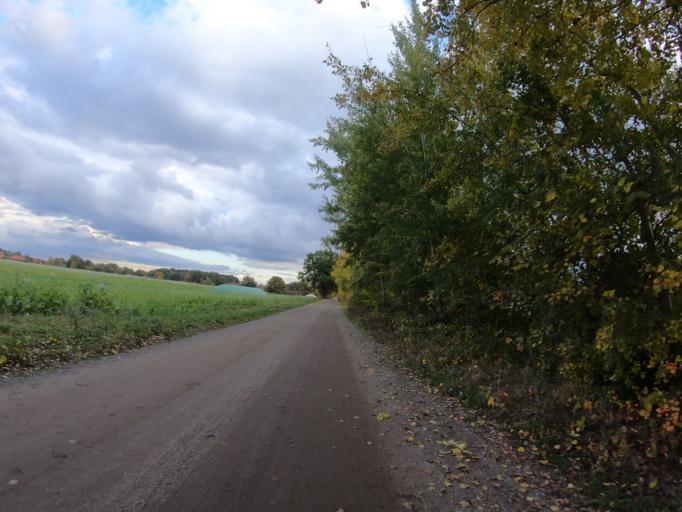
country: DE
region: Lower Saxony
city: Wagenhoff
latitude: 52.5231
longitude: 10.5240
